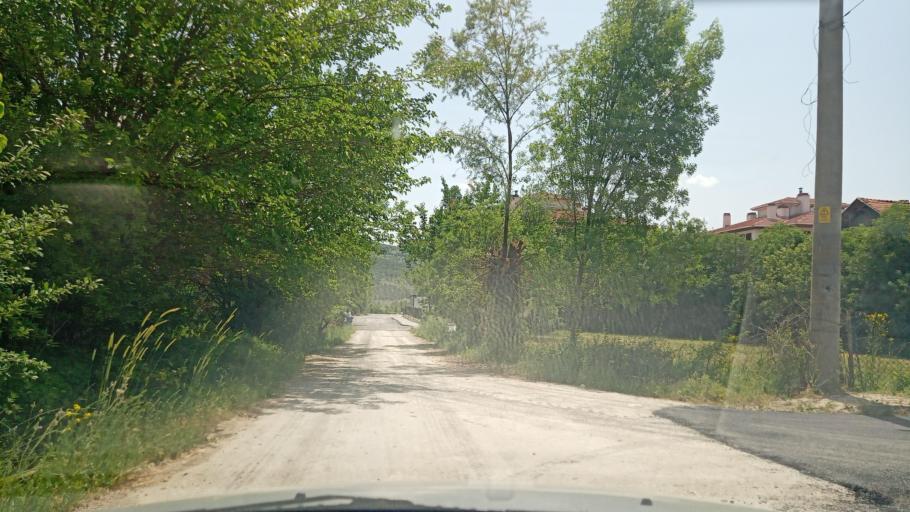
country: TR
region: Bolu
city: Seben
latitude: 40.4095
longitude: 31.5776
